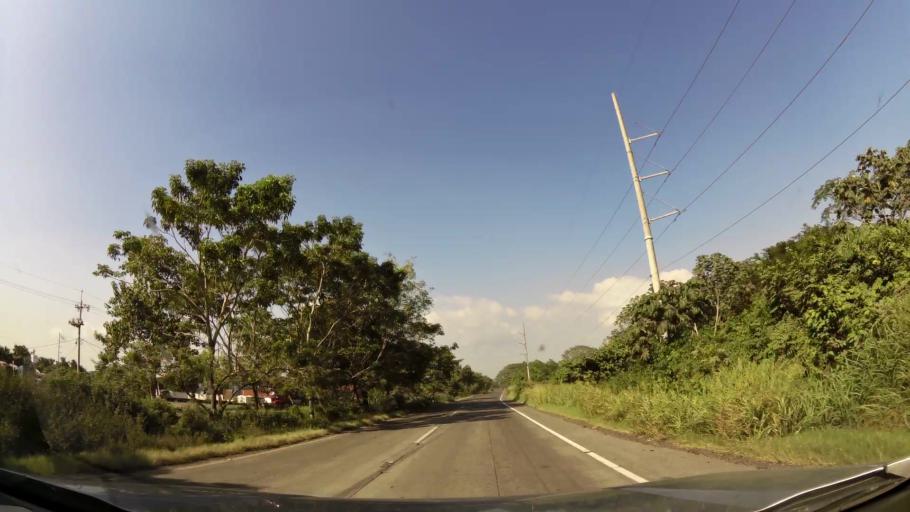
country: GT
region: Escuintla
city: Puerto San Jose
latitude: 13.9662
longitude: -90.7885
